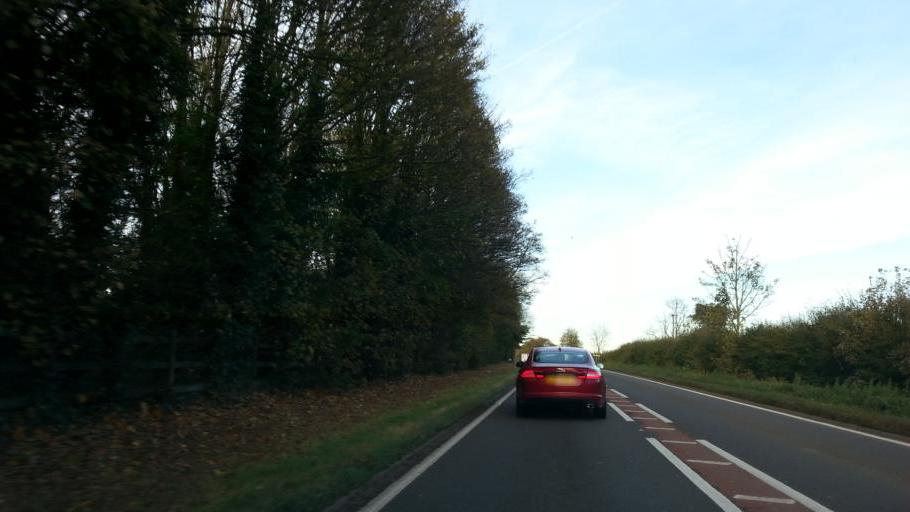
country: GB
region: England
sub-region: Northamptonshire
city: Northampton
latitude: 52.3018
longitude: -0.8248
